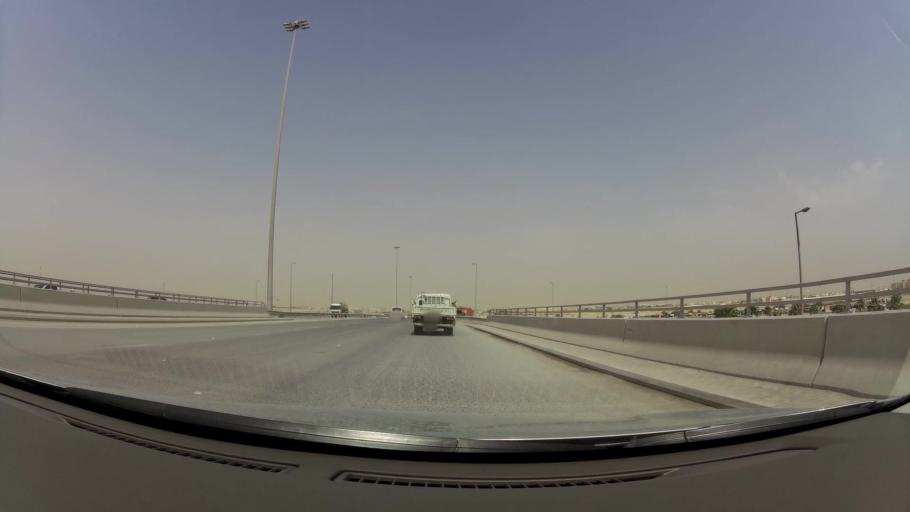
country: QA
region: Baladiyat ar Rayyan
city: Ar Rayyan
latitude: 25.2112
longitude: 51.4065
